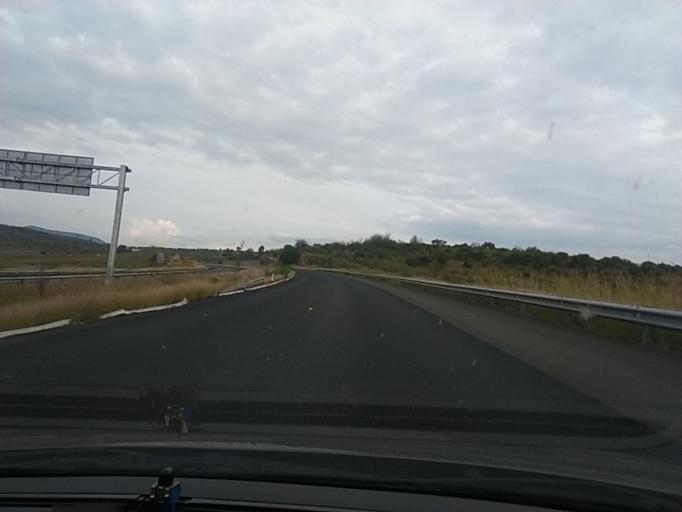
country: MX
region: Mexico
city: Huaniqueo de Morales
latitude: 19.8813
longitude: -101.5071
